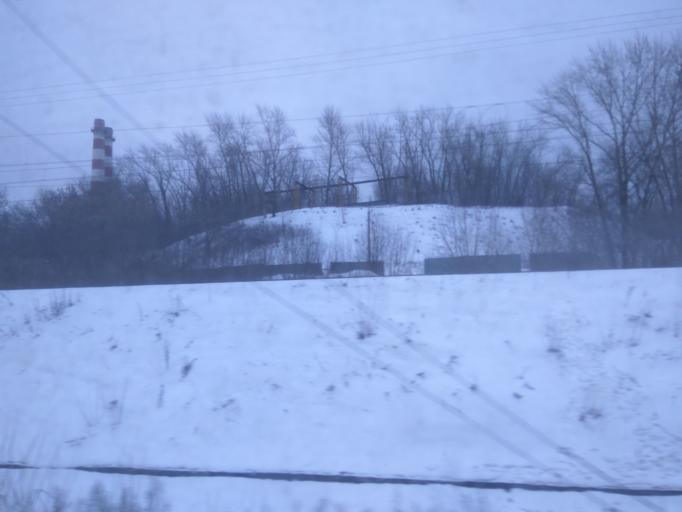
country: RU
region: Moskovskaya
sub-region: Podol'skiy Rayon
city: Podol'sk
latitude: 55.4571
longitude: 37.5636
